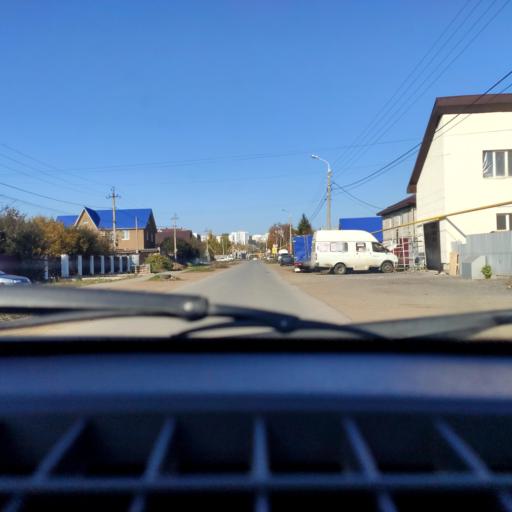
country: RU
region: Bashkortostan
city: Ufa
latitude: 54.7004
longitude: 55.9545
